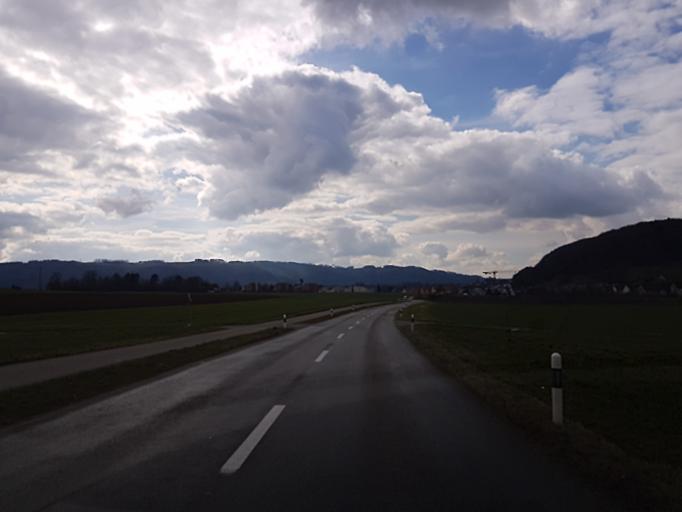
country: CH
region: Aargau
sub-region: Bezirk Baden
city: Wurenlos
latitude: 47.4462
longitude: 8.3796
